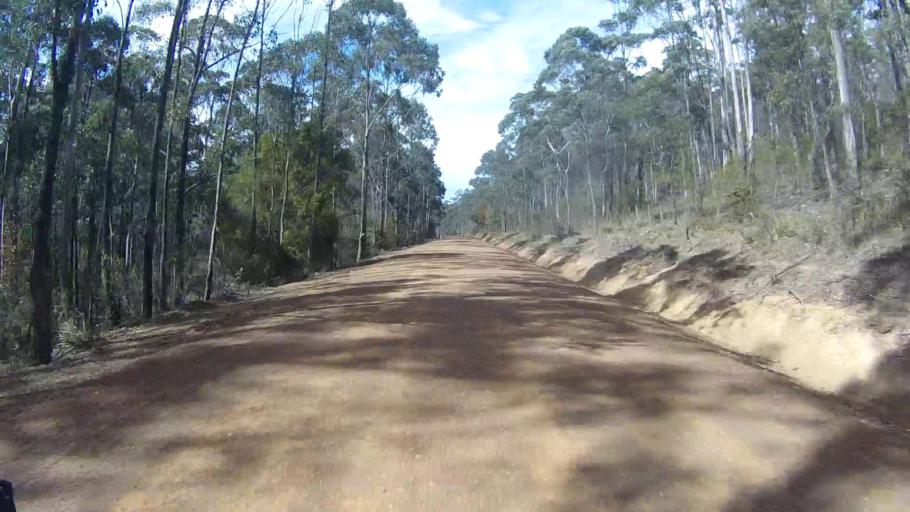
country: AU
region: Tasmania
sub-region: Sorell
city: Sorell
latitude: -42.6229
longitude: 147.9032
